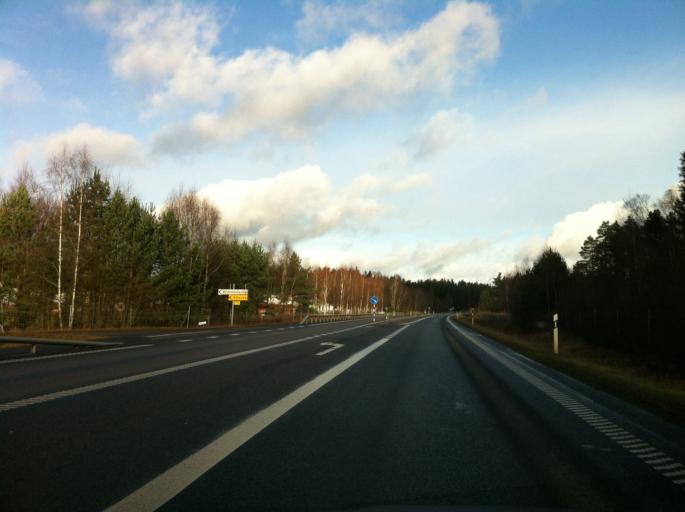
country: SE
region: Skane
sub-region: Osby Kommun
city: Osby
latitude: 56.3997
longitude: 14.0383
